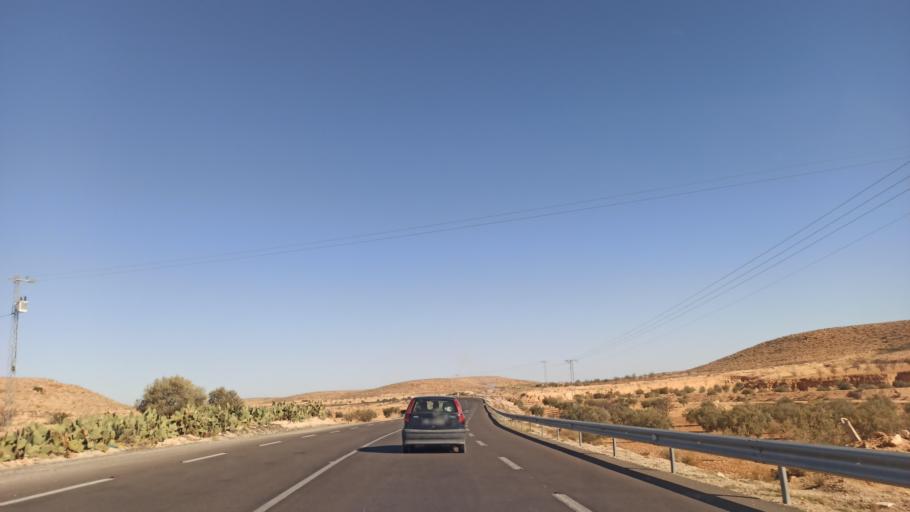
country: TN
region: Sidi Bu Zayd
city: Bi'r al Hufayy
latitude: 34.7157
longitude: 9.0551
